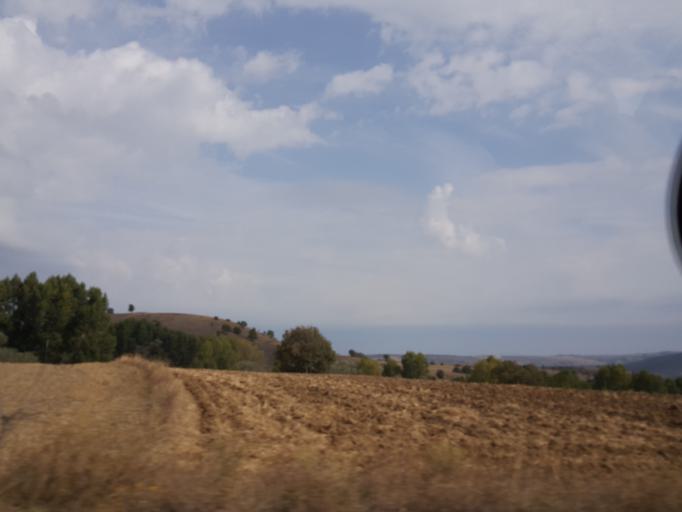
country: TR
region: Tokat
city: Zile
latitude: 40.3984
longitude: 35.8551
